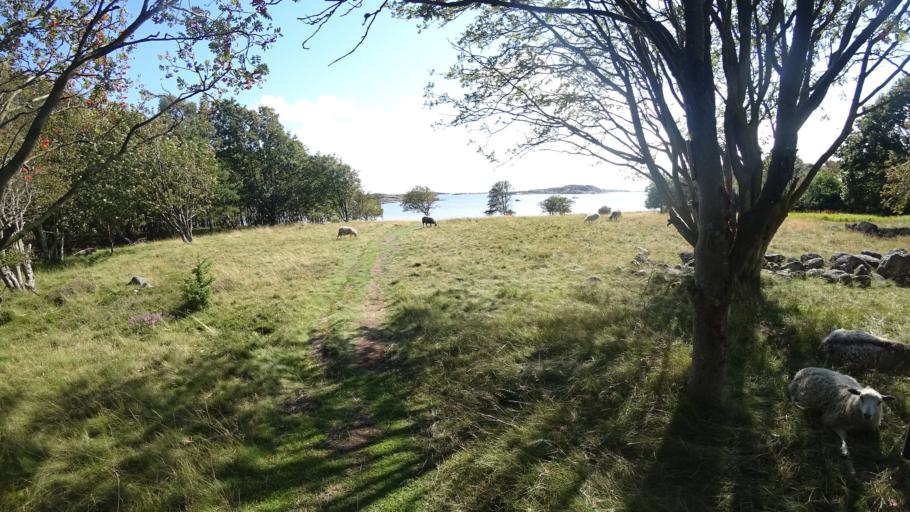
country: SE
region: Vaestra Goetaland
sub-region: Goteborg
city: Styrso
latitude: 57.6029
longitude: 11.7738
